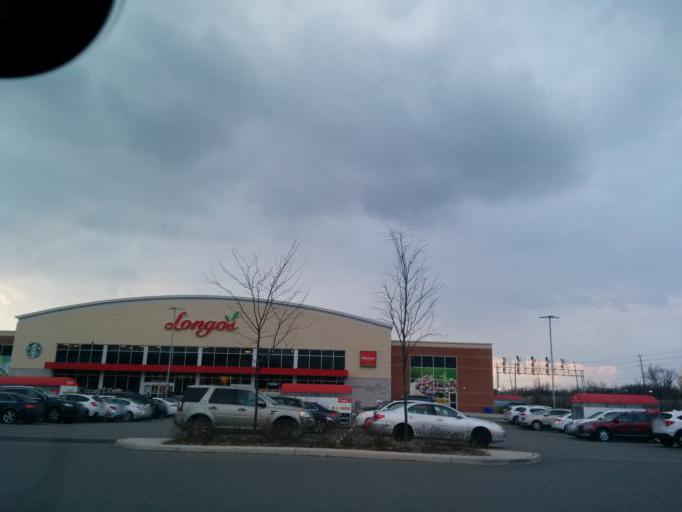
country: CA
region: Ontario
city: Oakville
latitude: 43.4628
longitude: -79.6747
